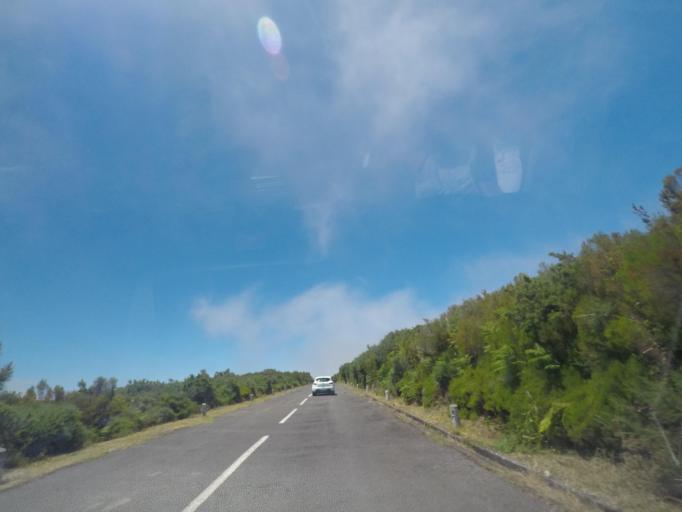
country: PT
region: Madeira
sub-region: Porto Moniz
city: Porto Moniz
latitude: 32.8057
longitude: -17.1919
